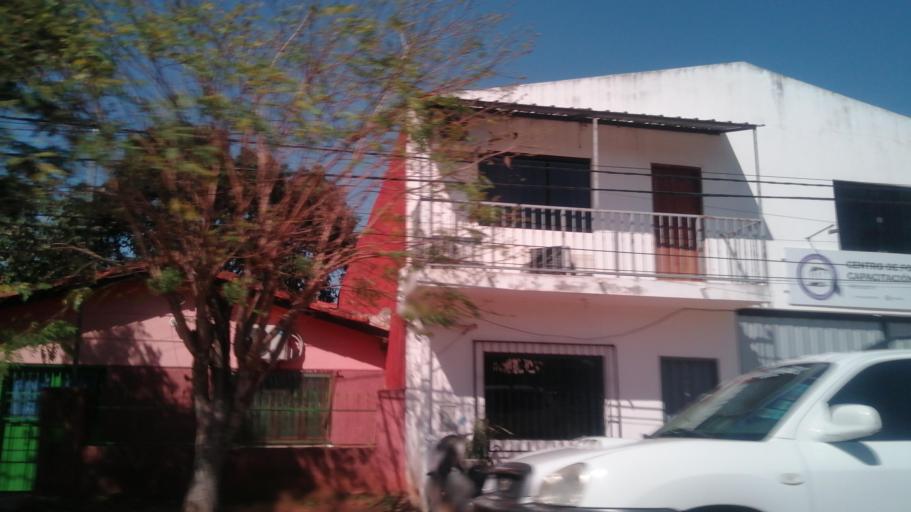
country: PY
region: Misiones
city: San Juan Bautista
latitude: -26.6722
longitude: -57.1337
